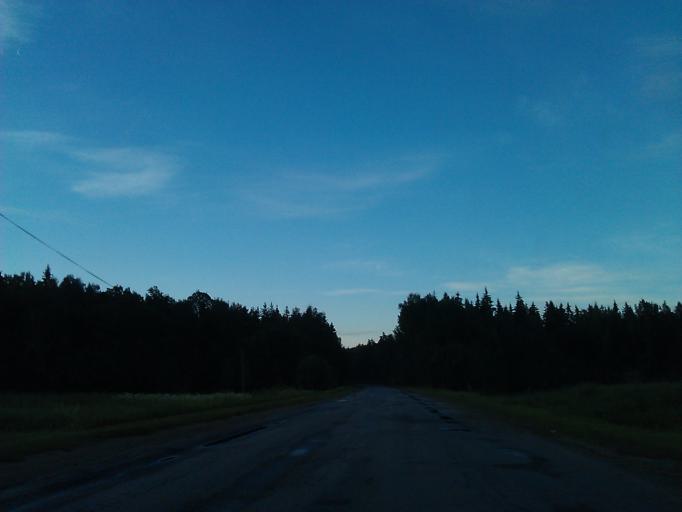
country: LV
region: Pargaujas
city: Stalbe
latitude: 57.3609
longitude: 25.0643
